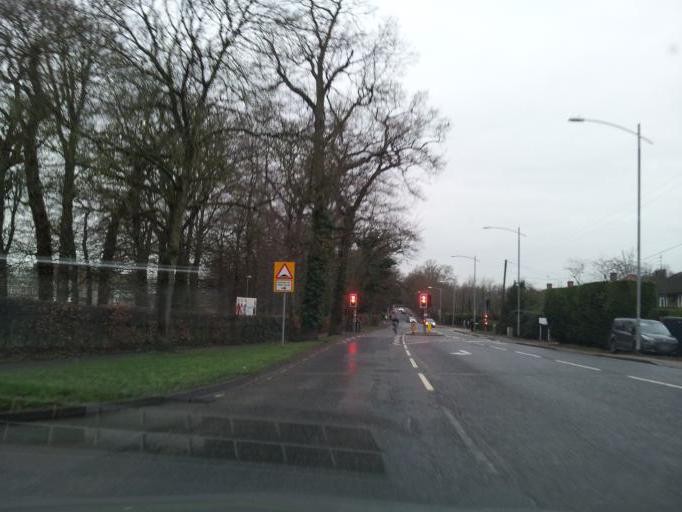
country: GB
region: England
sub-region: Cambridgeshire
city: Cambridge
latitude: 52.1792
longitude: 0.1356
